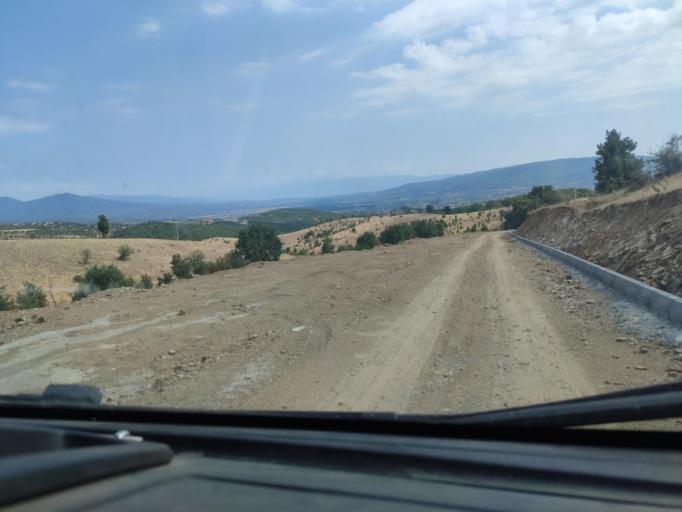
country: MK
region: Radovis
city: Radovish
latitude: 41.6717
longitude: 22.4046
